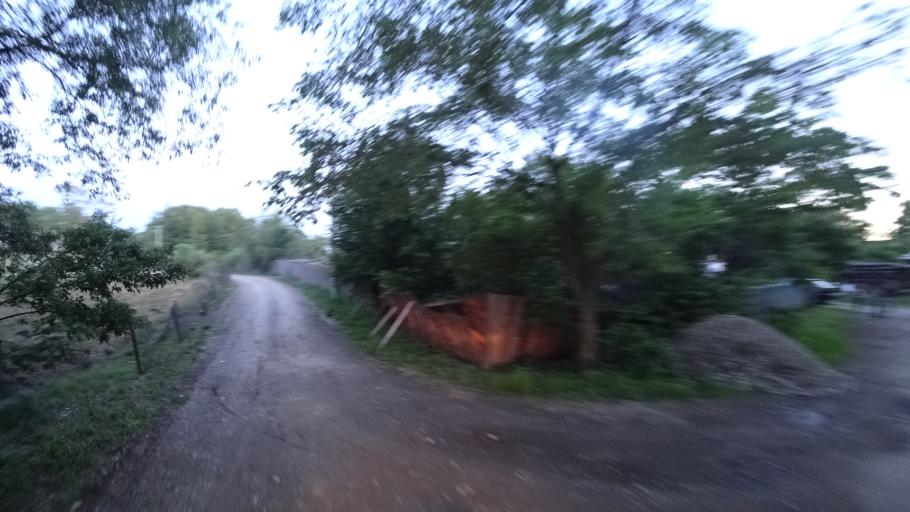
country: RU
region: Khabarovsk Krai
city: Khor
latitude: 47.8572
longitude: 134.9366
